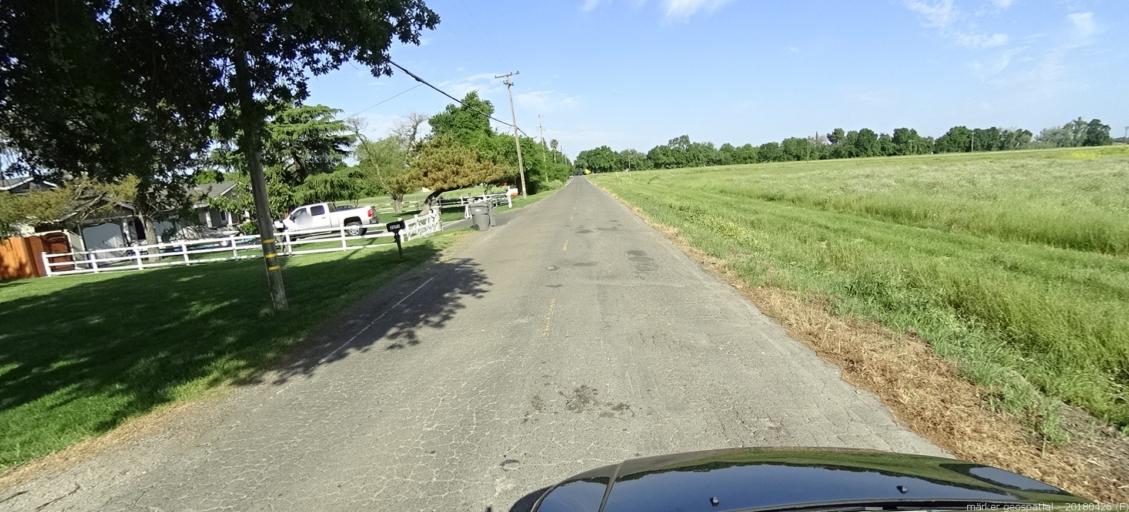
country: US
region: California
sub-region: Yolo County
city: West Sacramento
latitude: 38.5309
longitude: -121.5407
